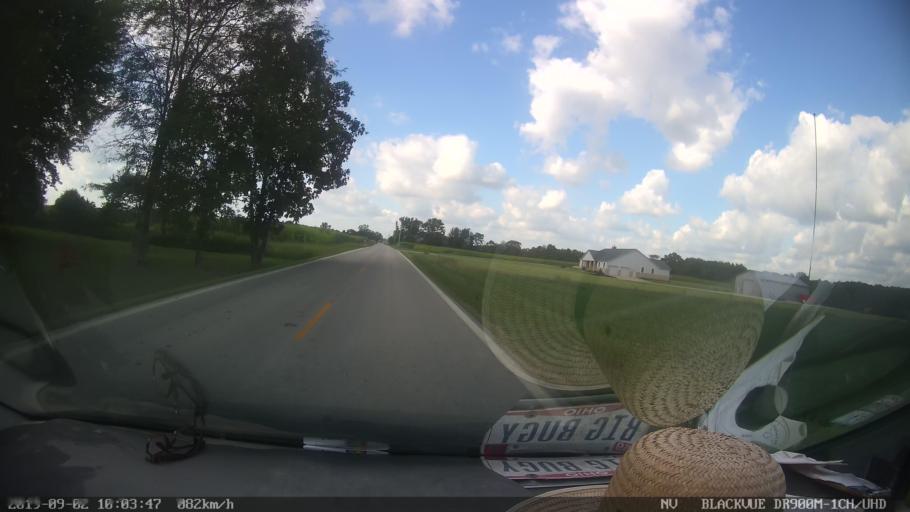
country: US
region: Ohio
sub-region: Delaware County
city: Ashley
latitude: 40.4784
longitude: -82.9612
